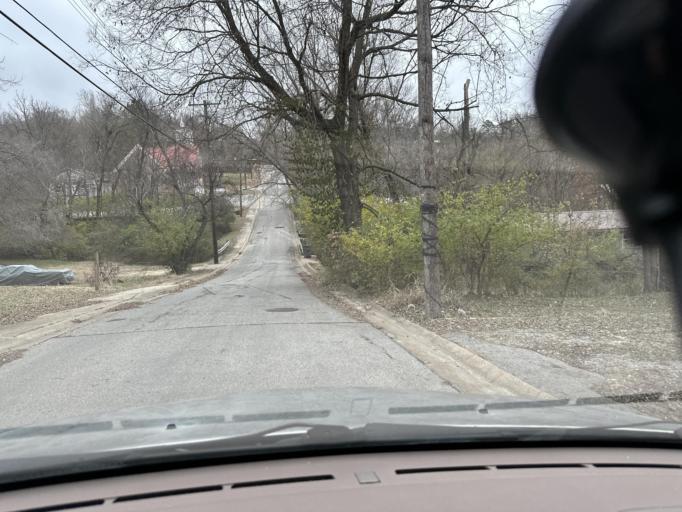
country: US
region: Arkansas
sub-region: Washington County
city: Fayetteville
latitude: 36.0626
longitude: -94.1560
